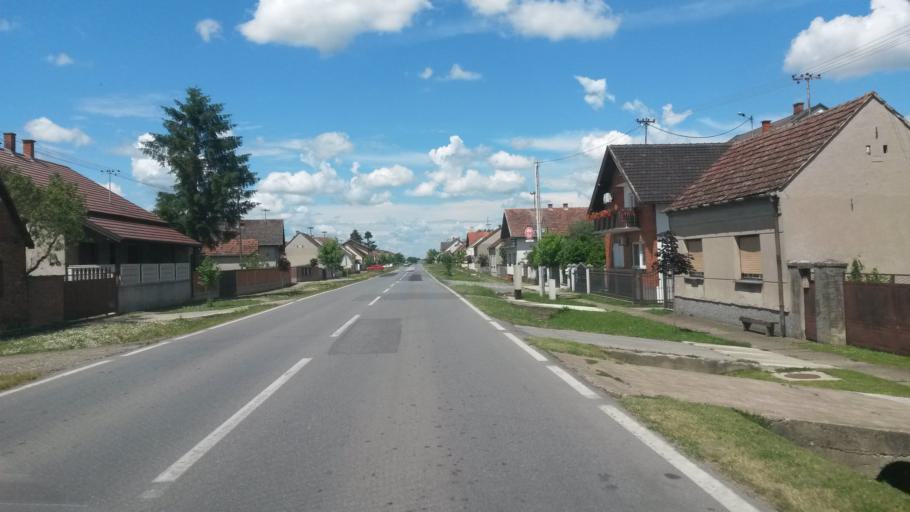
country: HR
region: Osjecko-Baranjska
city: Viskovci
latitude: 45.3511
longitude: 18.4234
